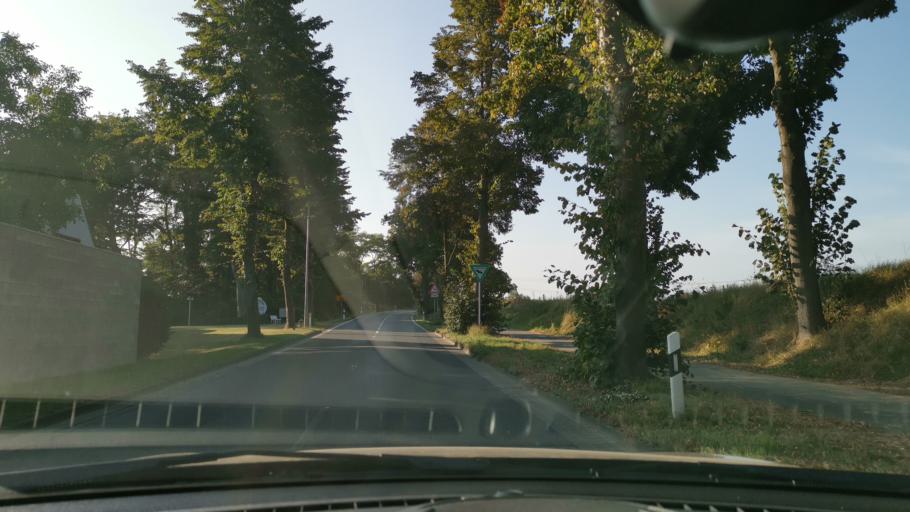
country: DE
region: North Rhine-Westphalia
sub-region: Regierungsbezirk Dusseldorf
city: Rommerskirchen
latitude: 51.0988
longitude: 6.7192
